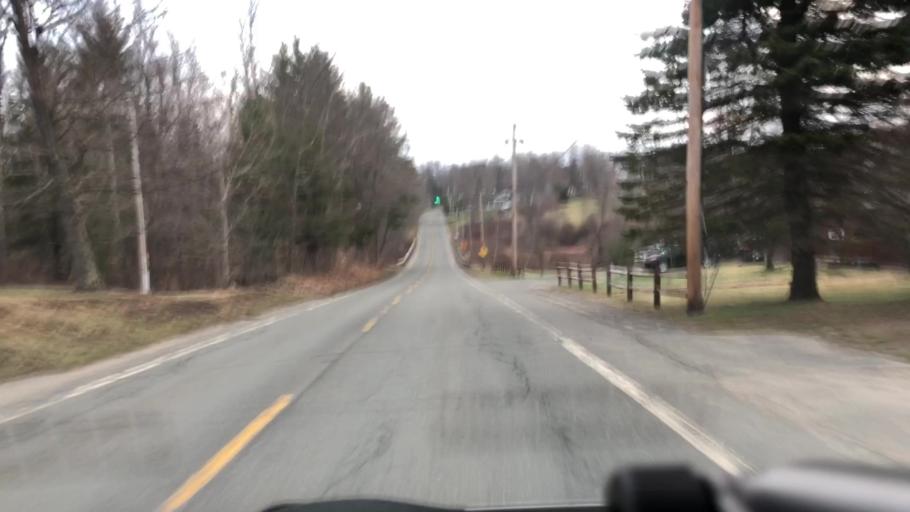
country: US
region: Massachusetts
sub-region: Hampshire County
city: Chesterfield
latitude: 42.4066
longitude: -72.9378
